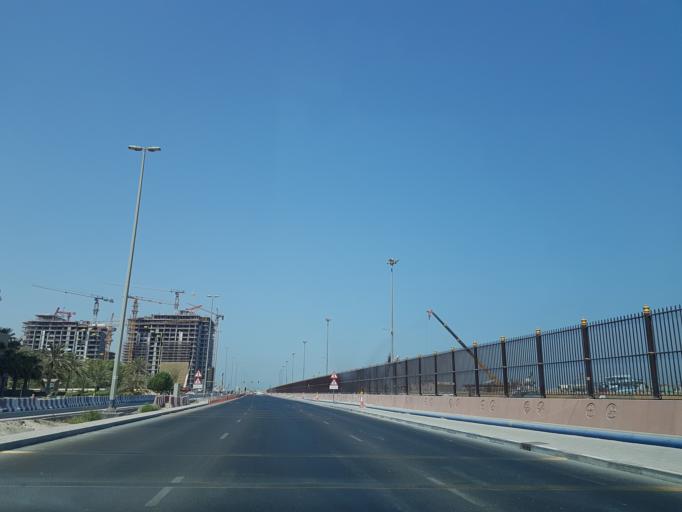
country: AE
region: Ash Shariqah
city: Sharjah
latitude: 25.2800
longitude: 55.3046
